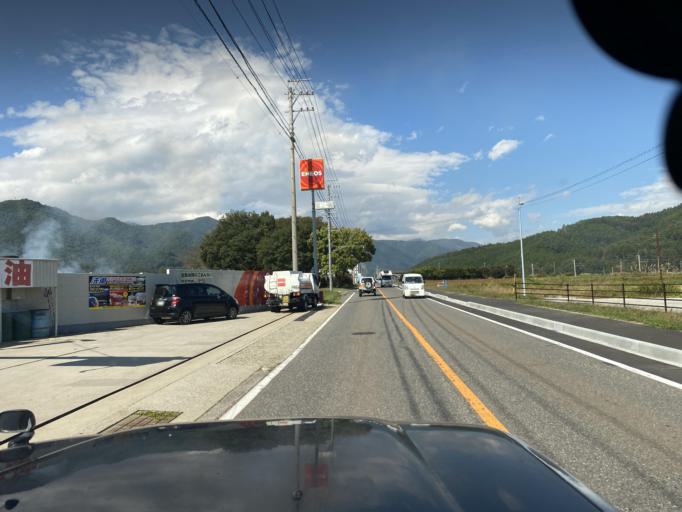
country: JP
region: Nagano
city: Omachi
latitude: 36.5302
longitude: 137.8481
